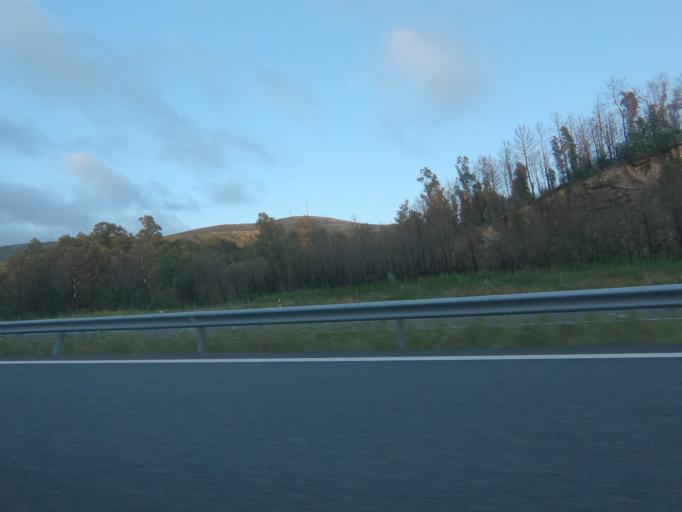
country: ES
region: Galicia
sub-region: Provincia de Pontevedra
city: Covelo
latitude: 42.1622
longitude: -8.3938
